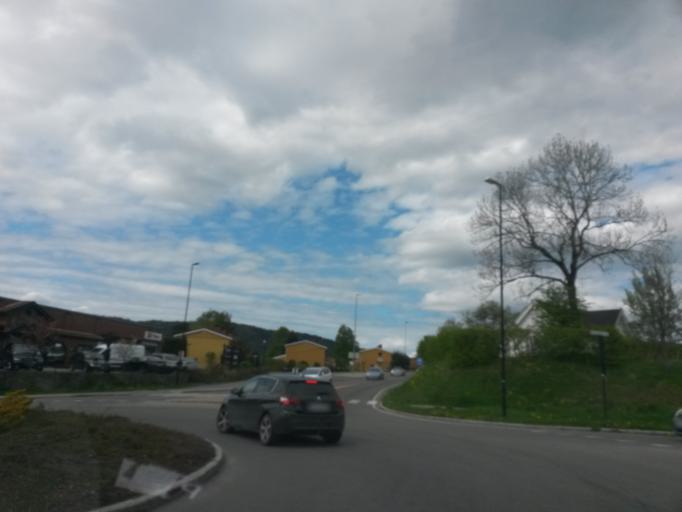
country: NO
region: Akershus
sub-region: Asker
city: Asker
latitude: 59.8380
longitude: 10.4348
